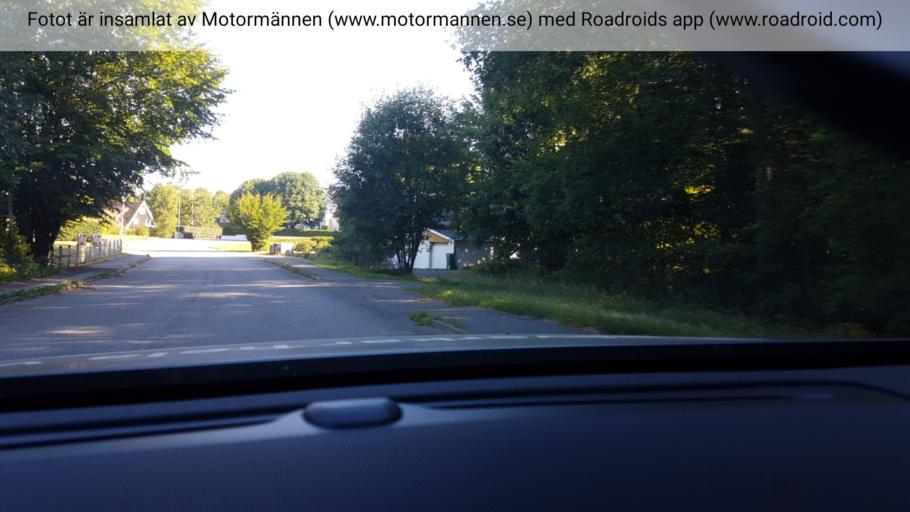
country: SE
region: Skane
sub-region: Hassleholms Kommun
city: Bjarnum
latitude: 56.3335
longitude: 13.6721
